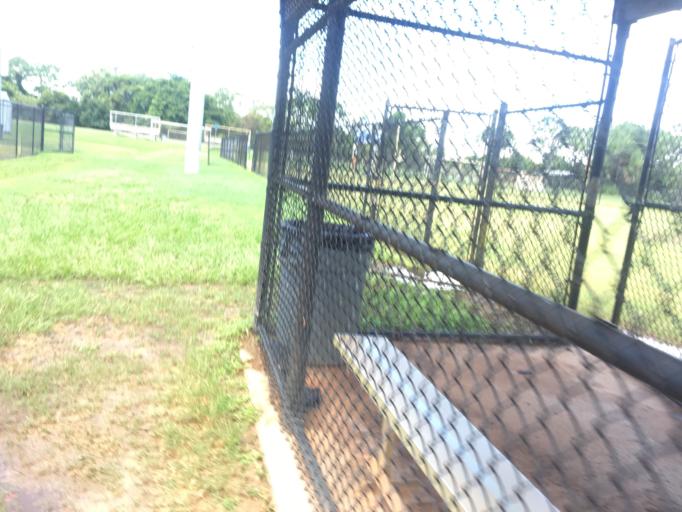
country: US
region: Florida
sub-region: Martin County
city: Palm City
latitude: 27.1781
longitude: -80.2728
